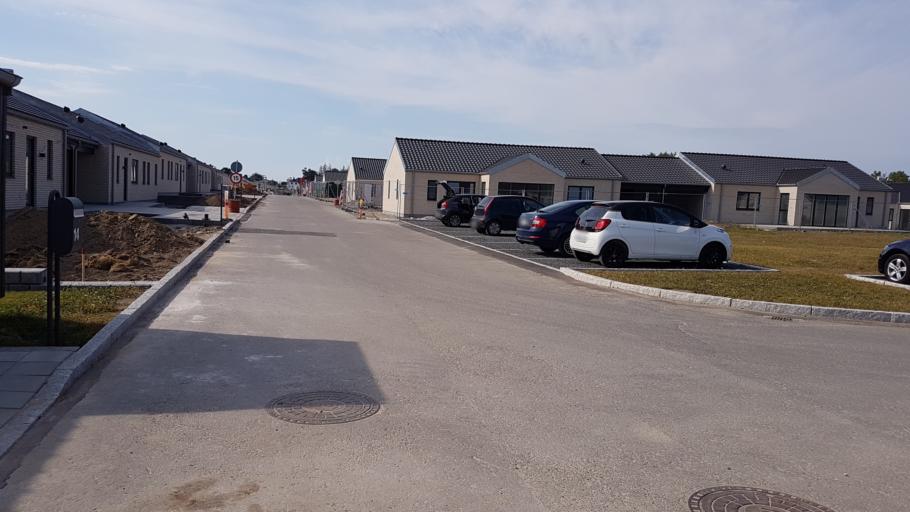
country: DK
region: Zealand
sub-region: Roskilde Kommune
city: Jyllinge
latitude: 55.7611
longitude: 12.1225
